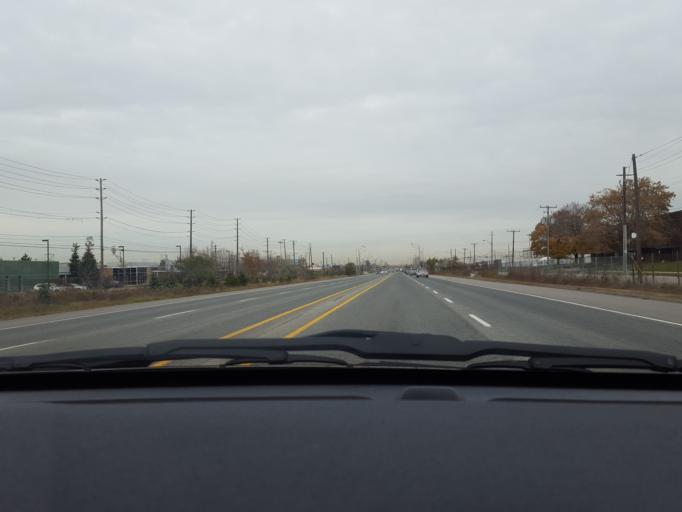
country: CA
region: Ontario
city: Etobicoke
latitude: 43.6947
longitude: -79.5851
